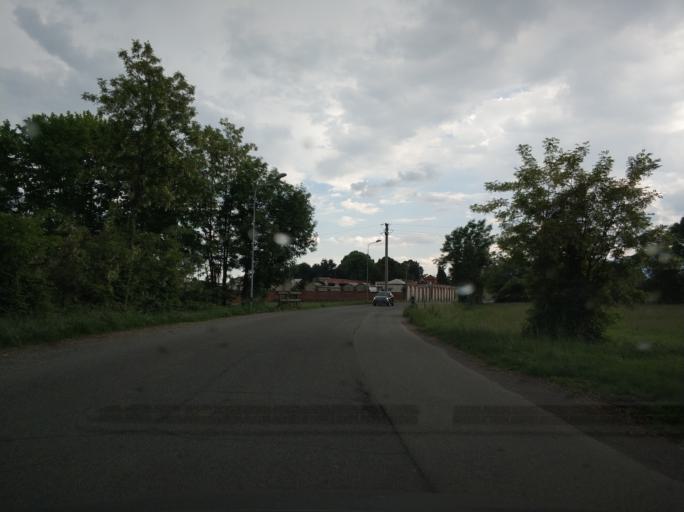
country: IT
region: Piedmont
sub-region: Provincia di Torino
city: Mathi
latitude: 45.2654
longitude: 7.5477
